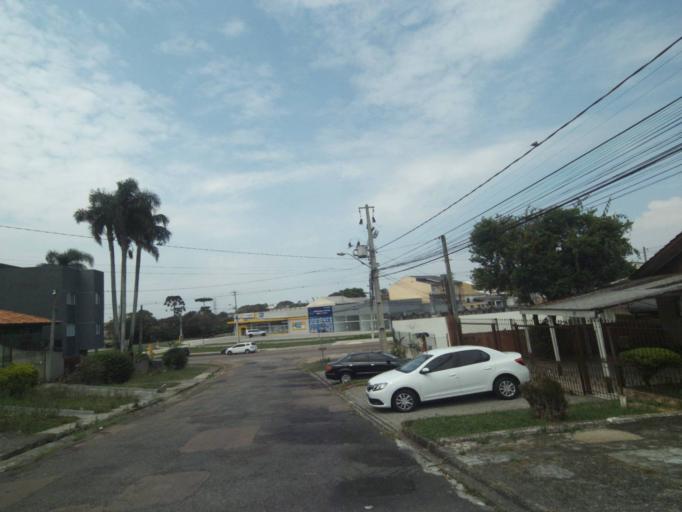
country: BR
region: Parana
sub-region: Curitiba
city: Curitiba
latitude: -25.4745
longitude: -49.3191
